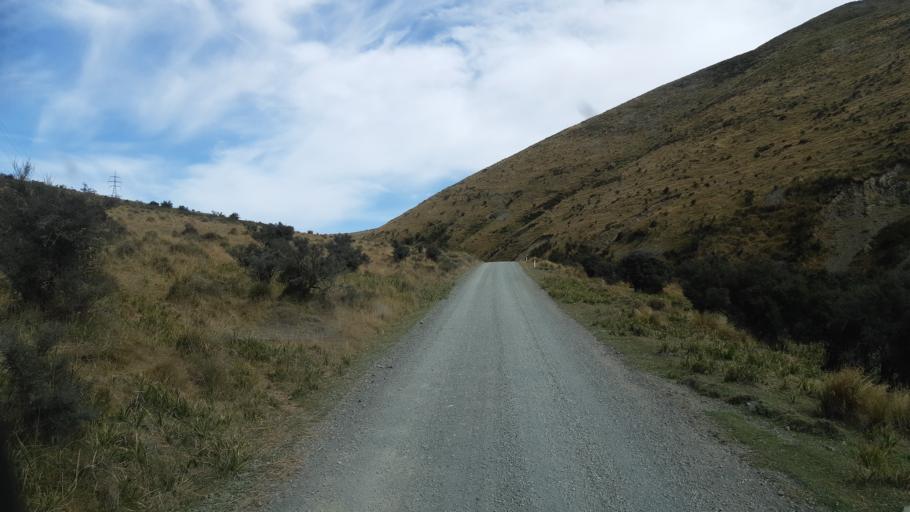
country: NZ
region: Canterbury
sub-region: Timaru District
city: Pleasant Point
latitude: -44.1929
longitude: 170.6218
